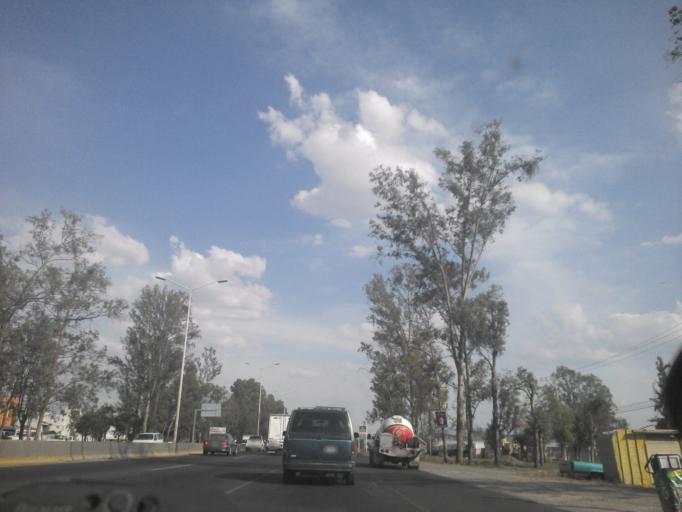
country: MX
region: Jalisco
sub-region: San Pedro Tlaquepaque
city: Paseo del Prado
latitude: 20.5967
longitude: -103.3910
